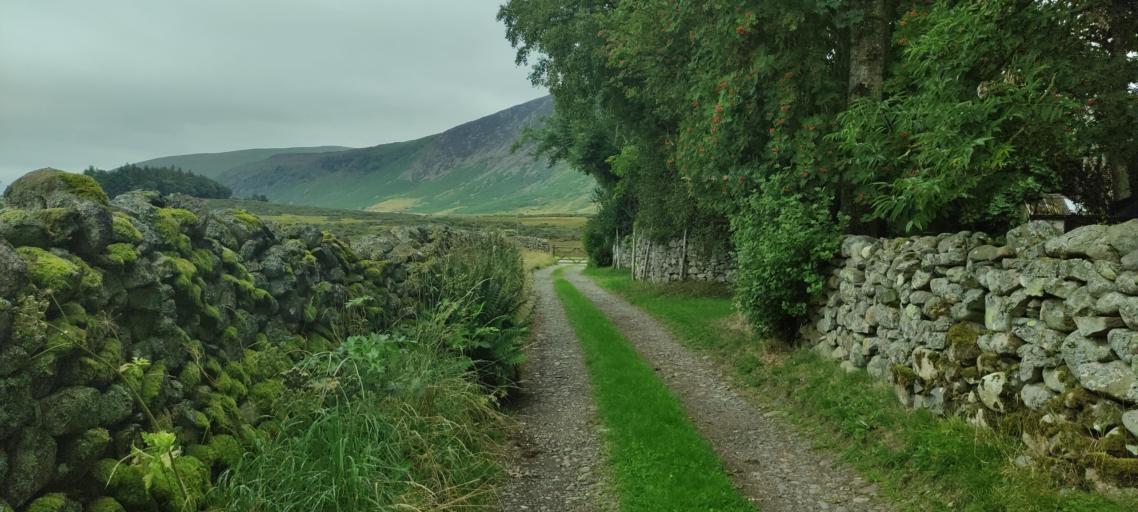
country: GB
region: England
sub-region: Cumbria
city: Keswick
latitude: 54.7104
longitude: -2.9978
